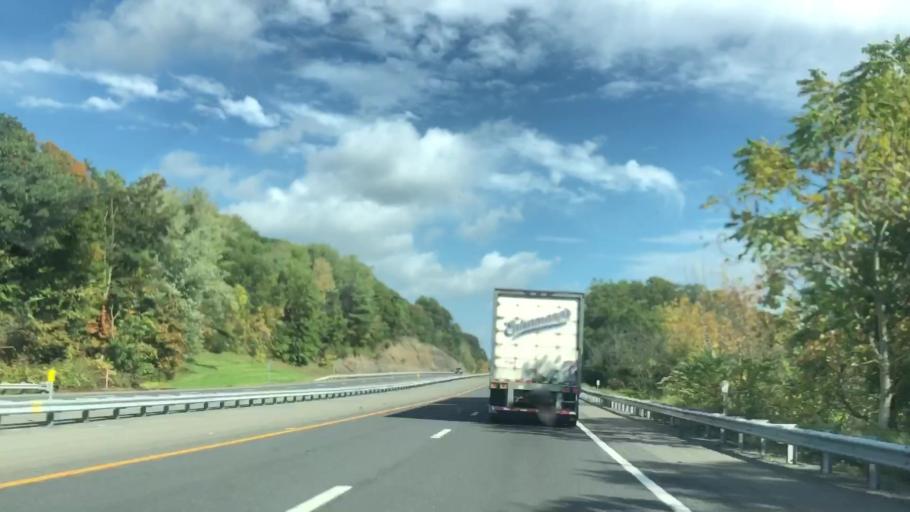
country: US
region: New York
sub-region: Ulster County
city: Lake Katrine
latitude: 41.9814
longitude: -74.0092
